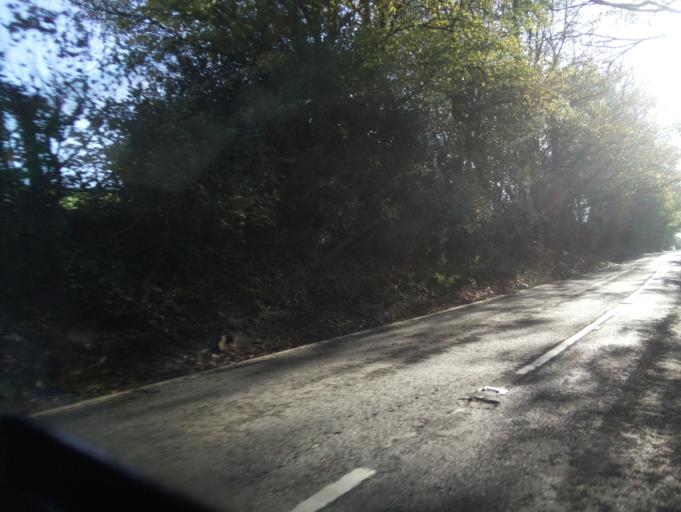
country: GB
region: England
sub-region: Dorset
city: Sherborne
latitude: 50.8441
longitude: -2.4617
